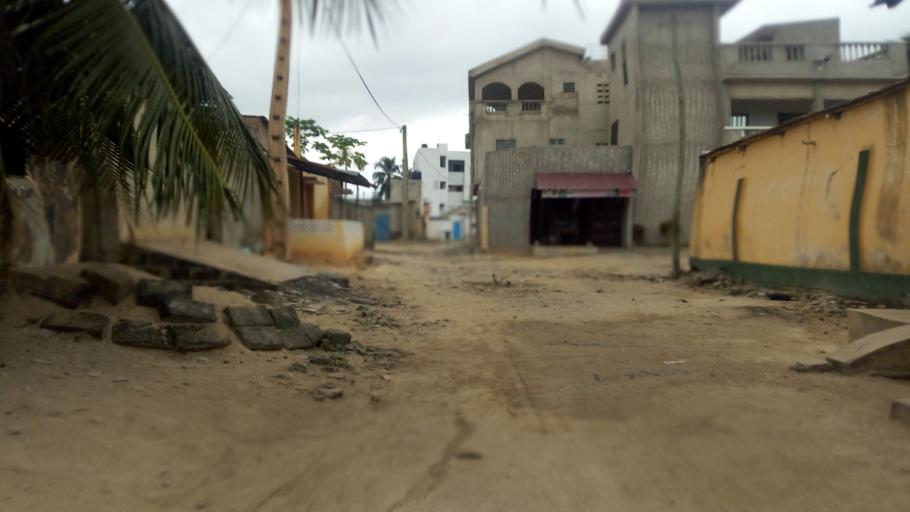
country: TG
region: Maritime
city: Lome
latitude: 6.1766
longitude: 1.1703
